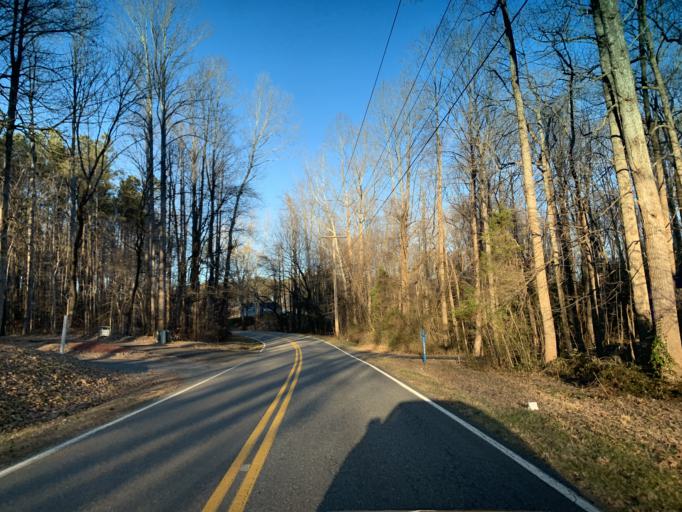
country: US
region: Maryland
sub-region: Saint Mary's County
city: Mechanicsville
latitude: 38.4561
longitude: -76.7098
